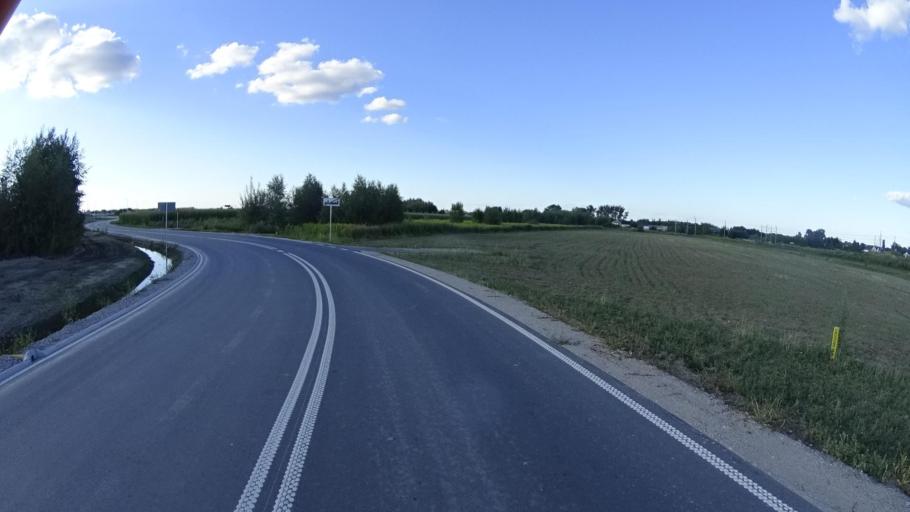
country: PL
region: Masovian Voivodeship
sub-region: Powiat piaseczynski
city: Mysiadlo
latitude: 52.1150
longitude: 20.9900
